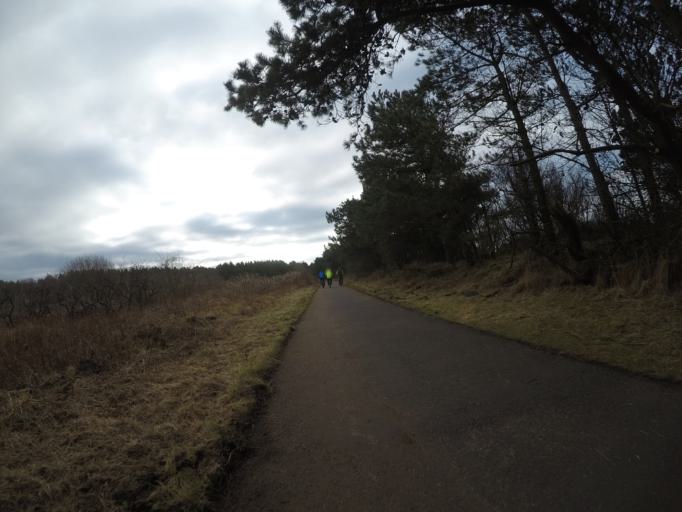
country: GB
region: Scotland
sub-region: North Ayrshire
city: Irvine
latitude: 55.5921
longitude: -4.6701
